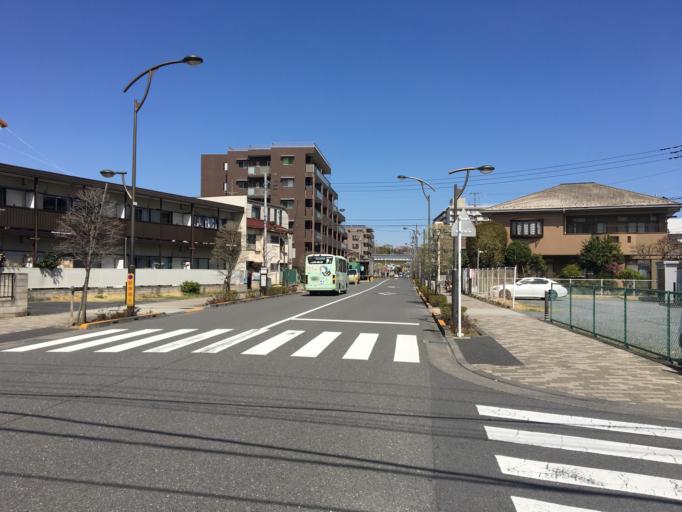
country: JP
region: Tokyo
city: Chofugaoka
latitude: 35.6602
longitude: 139.5467
